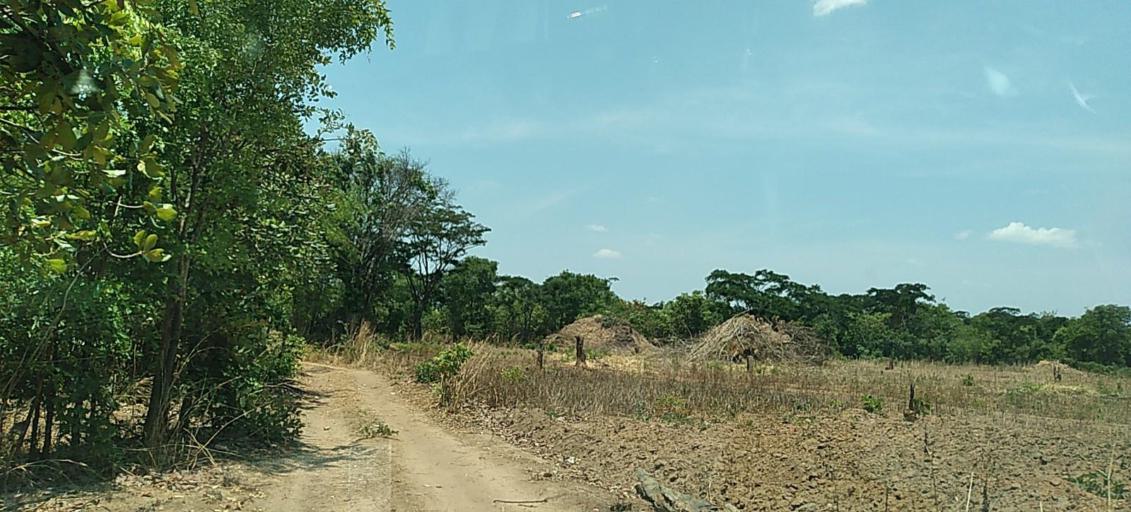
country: ZM
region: Copperbelt
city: Luanshya
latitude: -13.0650
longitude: 28.4056
